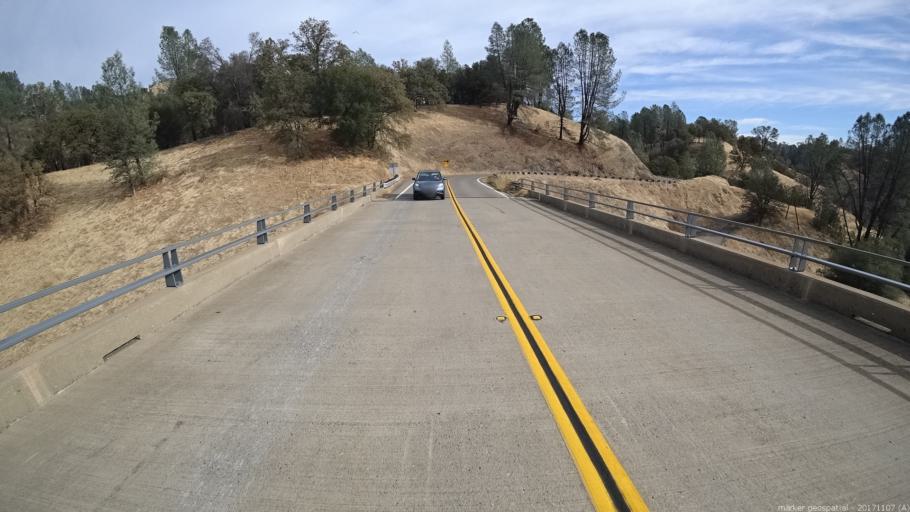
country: US
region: California
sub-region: Shasta County
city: Shasta
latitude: 40.5116
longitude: -122.5221
